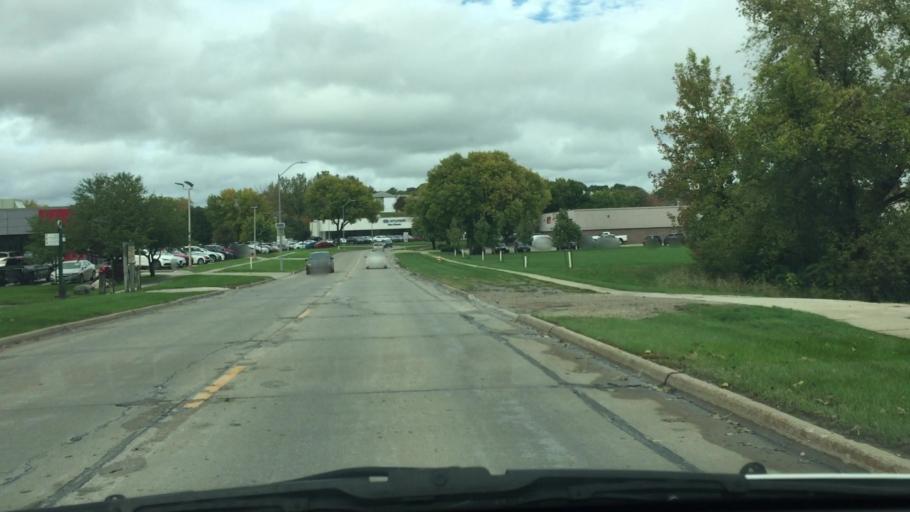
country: US
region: Iowa
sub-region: Polk County
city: Clive
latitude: 41.6112
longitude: -93.7749
